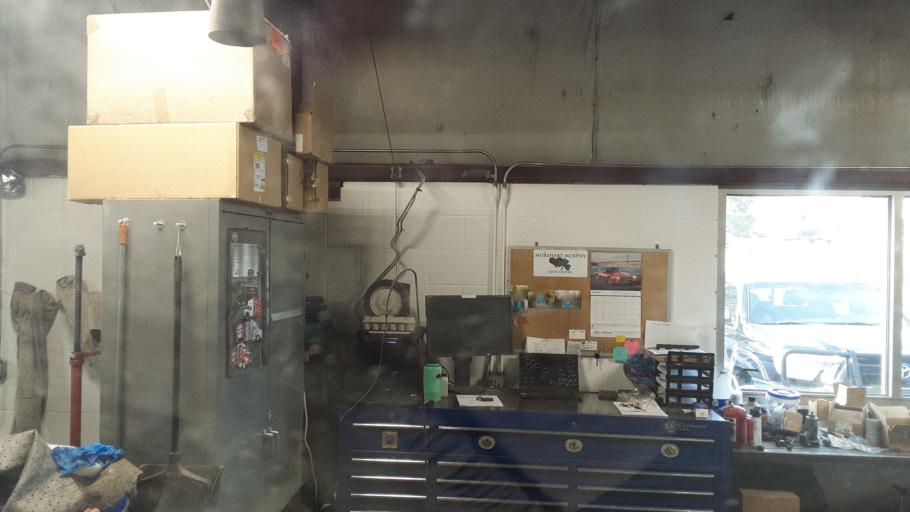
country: US
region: Colorado
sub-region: La Plata County
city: Durango
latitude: 37.2373
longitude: -107.8715
